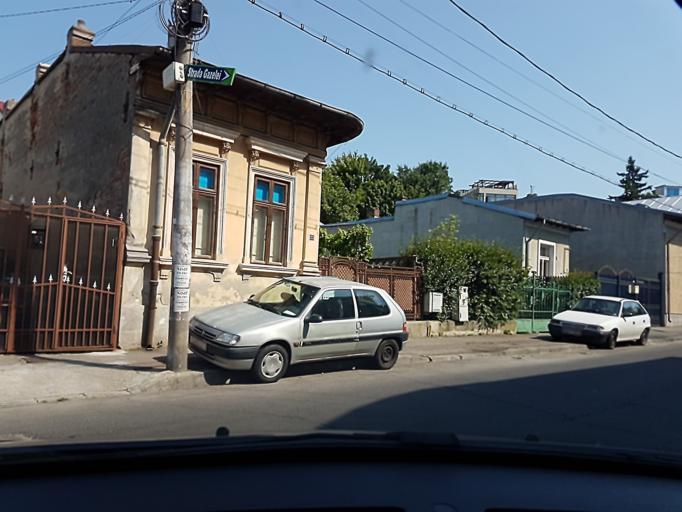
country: RO
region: Bucuresti
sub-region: Municipiul Bucuresti
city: Bucuresti
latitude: 44.4178
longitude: 26.0911
